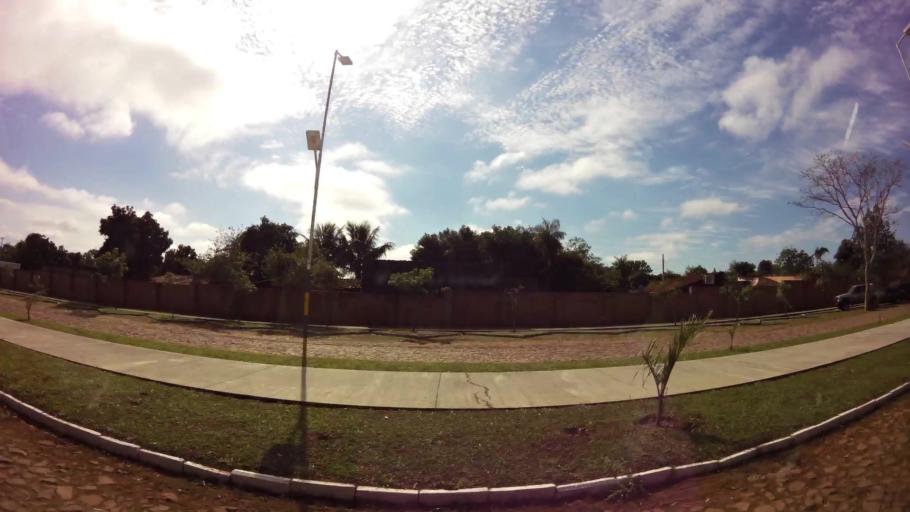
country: PY
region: Central
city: San Lorenzo
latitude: -25.2819
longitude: -57.4881
